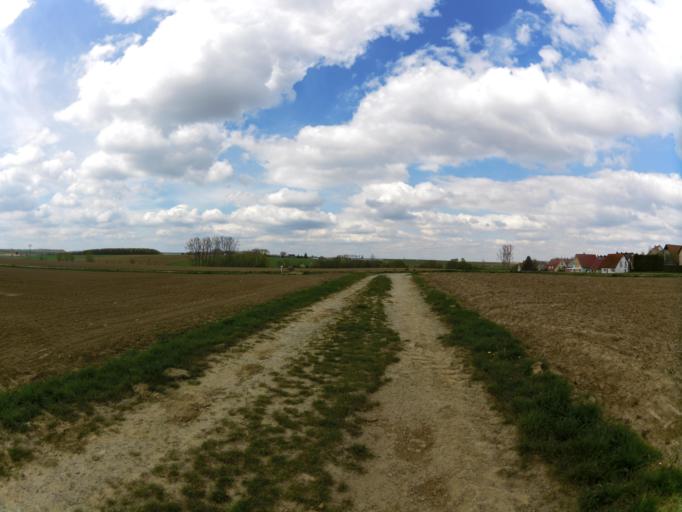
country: DE
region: Bavaria
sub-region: Regierungsbezirk Unterfranken
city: Giebelstadt
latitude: 49.6529
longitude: 9.9343
